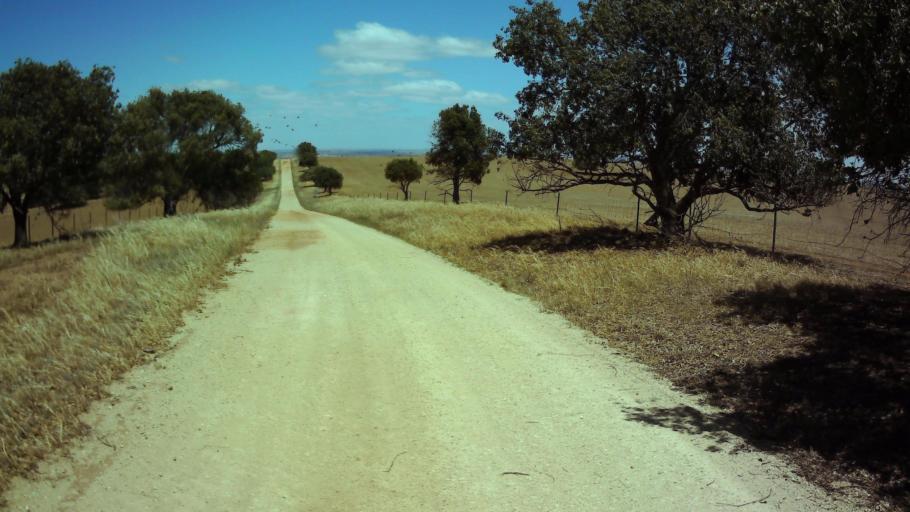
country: AU
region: New South Wales
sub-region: Weddin
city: Grenfell
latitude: -33.9537
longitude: 148.3659
